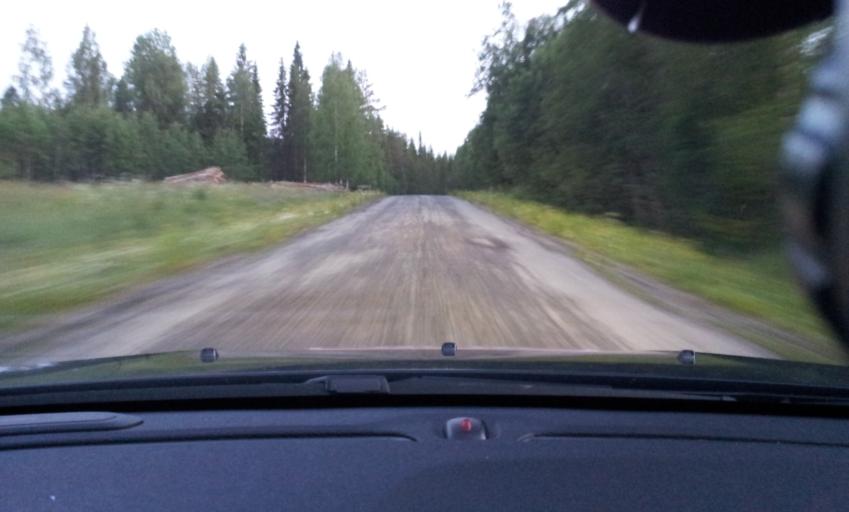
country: SE
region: Vaesternorrland
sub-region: Ange Kommun
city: Fransta
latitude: 62.7799
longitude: 15.9924
